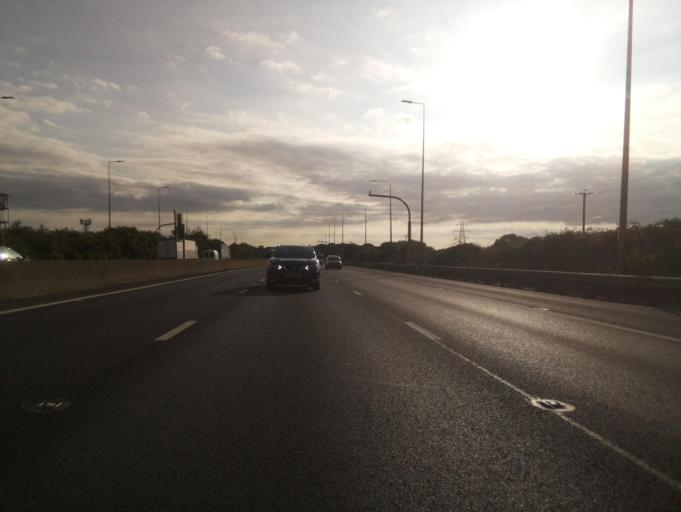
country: GB
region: England
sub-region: South Gloucestershire
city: Almondsbury
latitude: 51.5439
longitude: -2.5791
